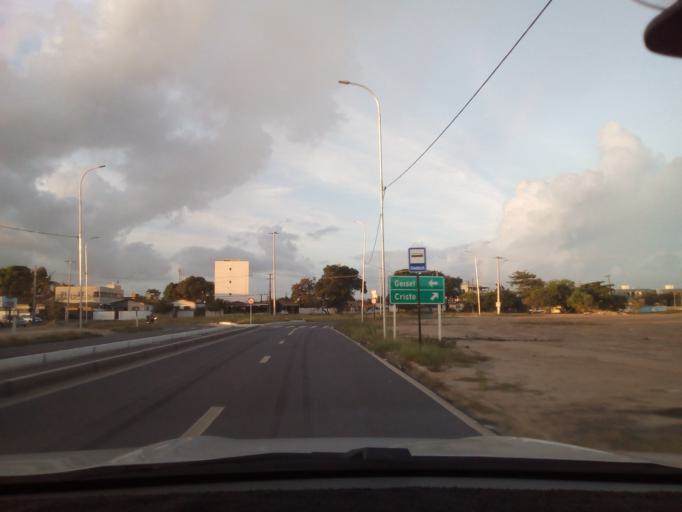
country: BR
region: Paraiba
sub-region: Joao Pessoa
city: Joao Pessoa
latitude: -7.1660
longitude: -34.8745
